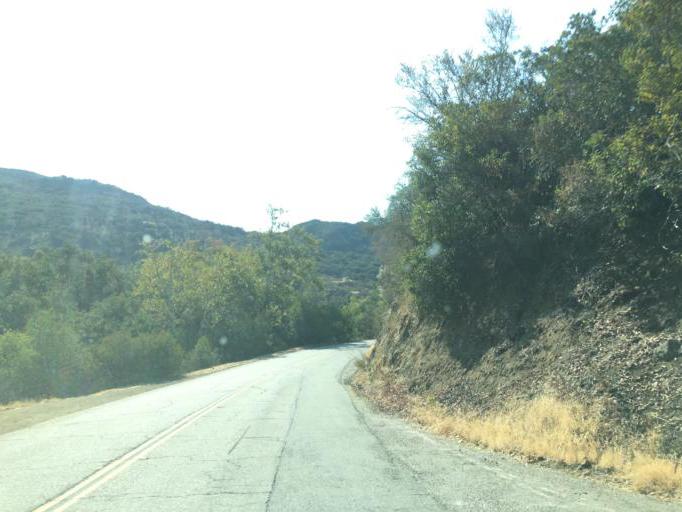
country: US
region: California
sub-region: Los Angeles County
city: Hidden Hills
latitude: 34.1087
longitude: -118.6637
